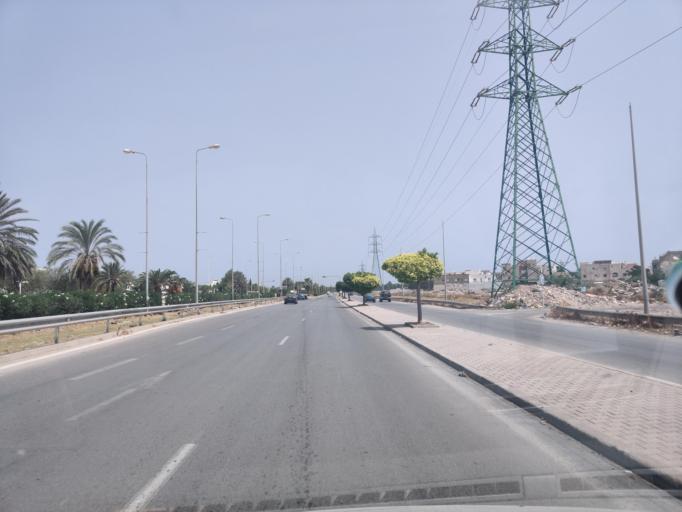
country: TN
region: Tunis
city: Carthage
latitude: 36.8502
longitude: 10.3054
